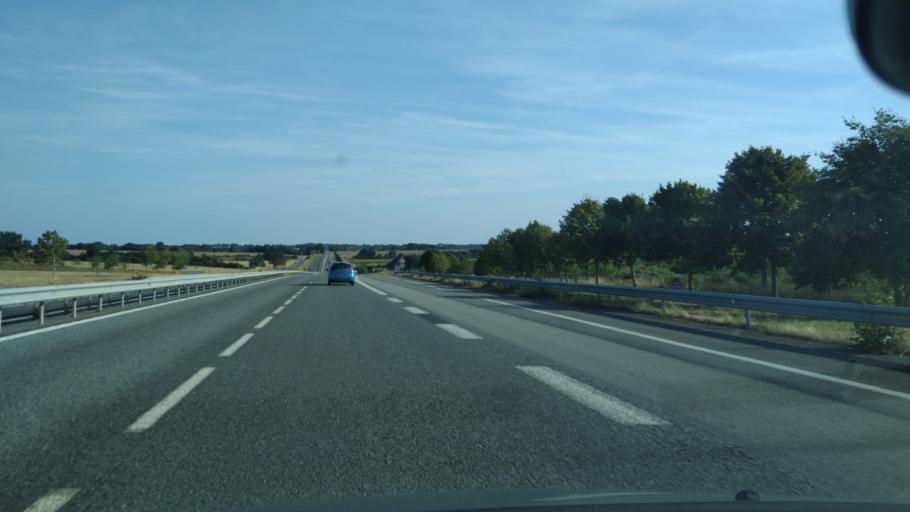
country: FR
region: Pays de la Loire
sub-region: Departement de la Mayenne
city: Entrammes
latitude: 47.9218
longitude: -0.6910
